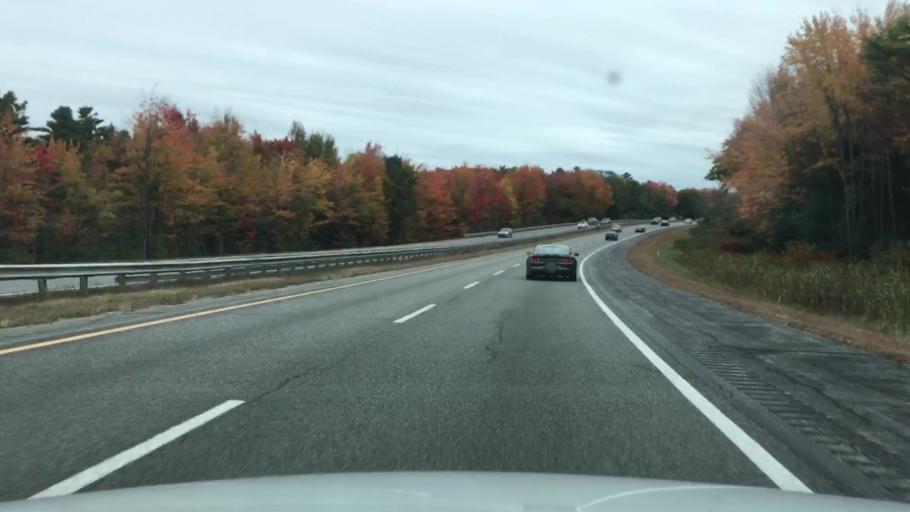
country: US
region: Maine
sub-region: Cumberland County
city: Freeport
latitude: 43.8981
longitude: -70.0769
